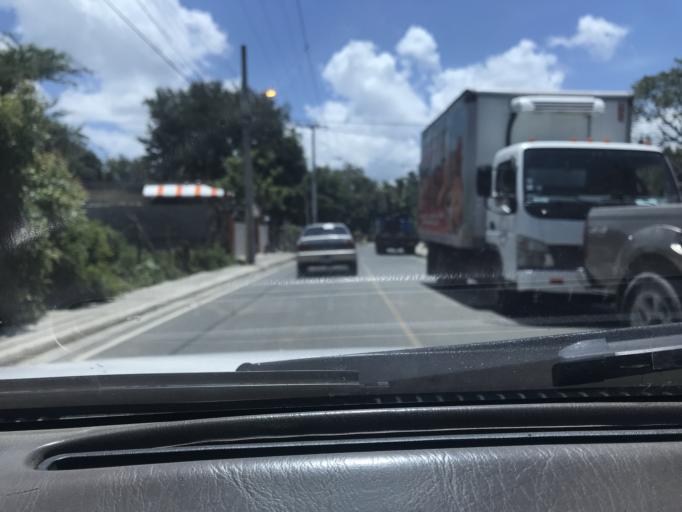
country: DO
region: Santiago
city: Santiago de los Caballeros
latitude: 19.4230
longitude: -70.7061
